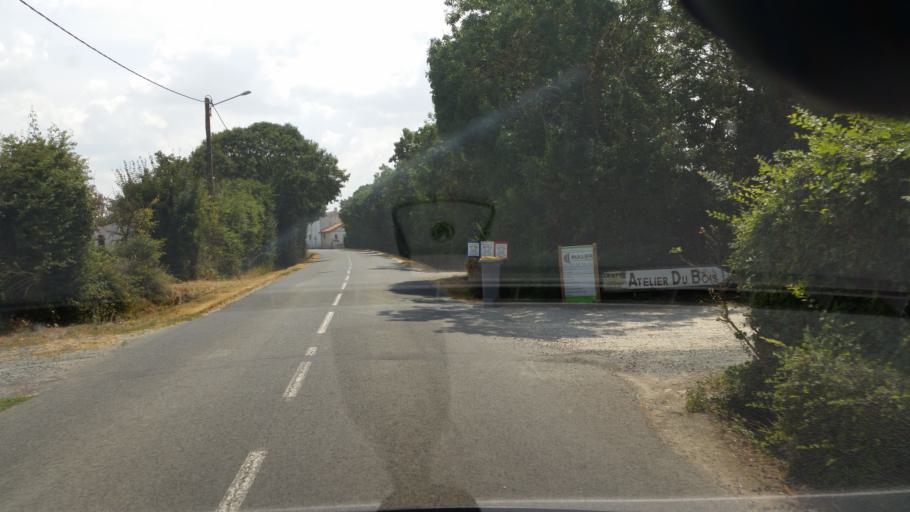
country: FR
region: Poitou-Charentes
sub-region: Departement de la Charente-Maritime
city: Saint-Jean-de-Liversay
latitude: 46.2144
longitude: -0.8822
